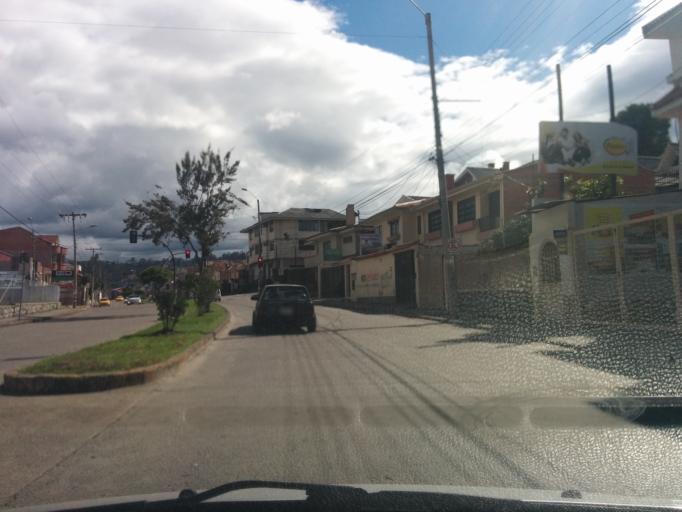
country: EC
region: Azuay
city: Cuenca
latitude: -2.9044
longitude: -78.9917
